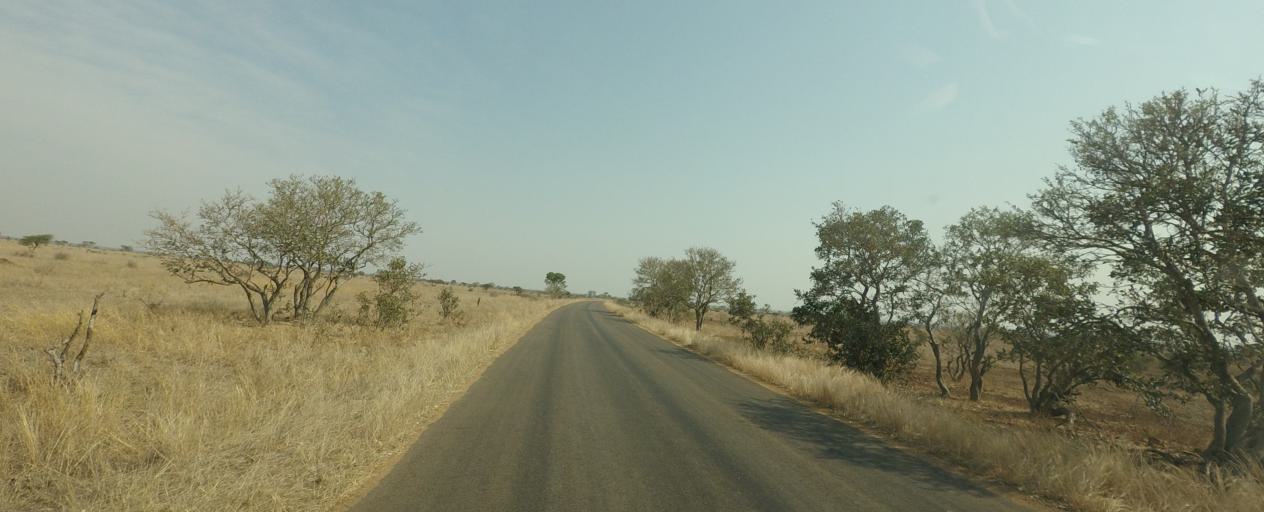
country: ZA
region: Limpopo
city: Thulamahashi
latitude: -24.3222
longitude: 31.7512
